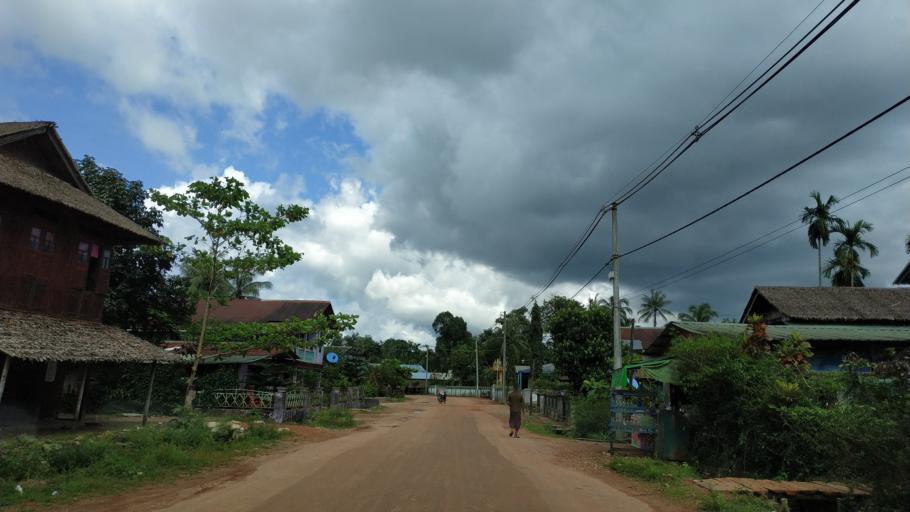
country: MM
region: Tanintharyi
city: Dawei
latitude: 14.2773
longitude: 98.1544
